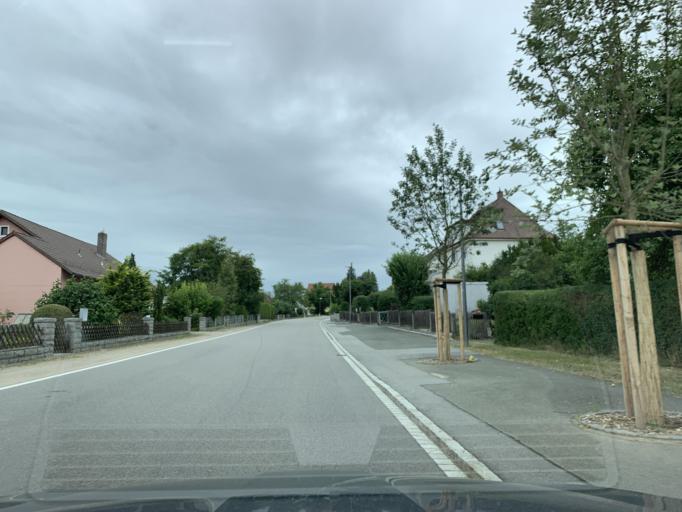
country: DE
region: Bavaria
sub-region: Upper Palatinate
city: Schwarzhofen
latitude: 49.3736
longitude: 12.3469
